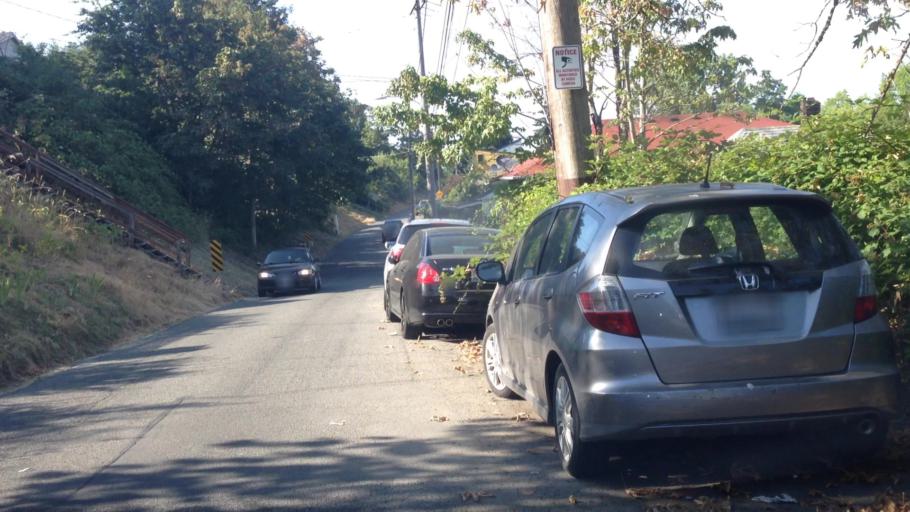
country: US
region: Washington
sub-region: King County
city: Seattle
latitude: 47.5645
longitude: -122.2889
